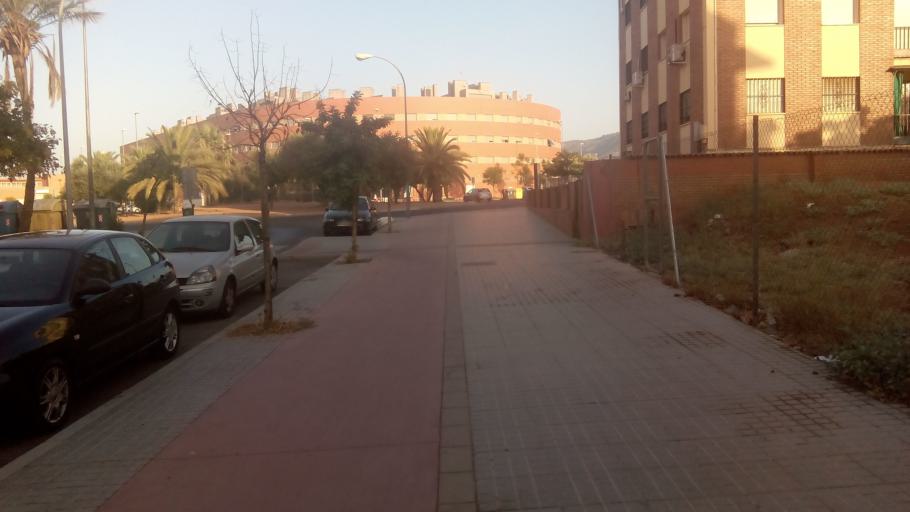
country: ES
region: Andalusia
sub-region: Province of Cordoba
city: Cordoba
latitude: 37.8961
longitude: -4.7864
